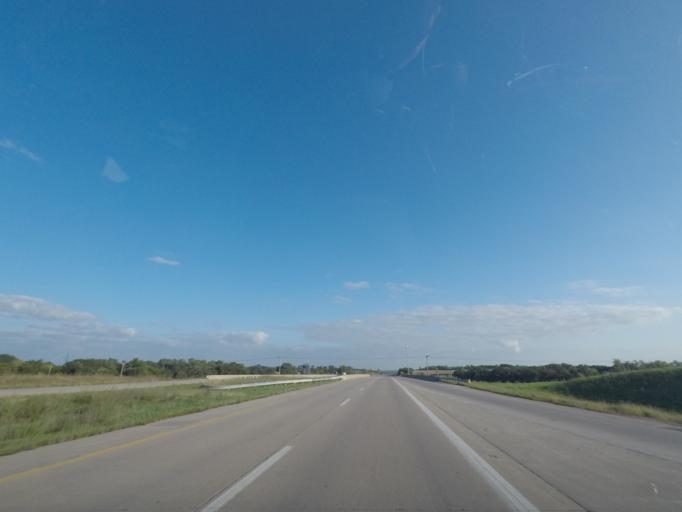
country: US
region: Iowa
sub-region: Warren County
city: Carlisle
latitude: 41.5238
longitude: -93.5194
